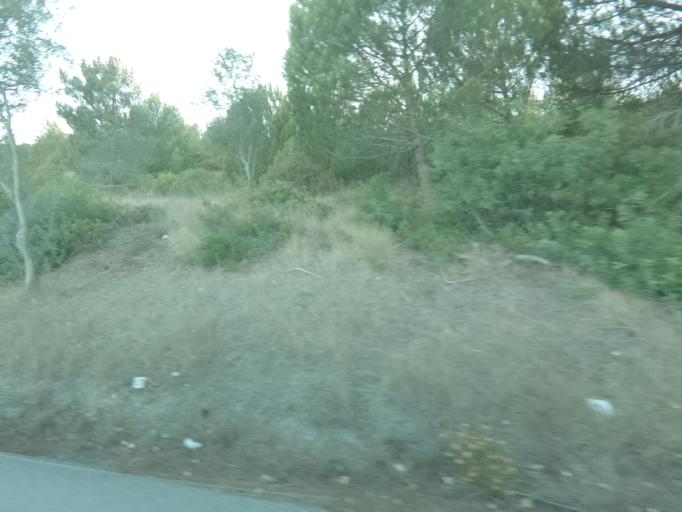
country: PT
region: Setubal
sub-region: Palmela
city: Quinta do Anjo
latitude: 38.5254
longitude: -8.9826
